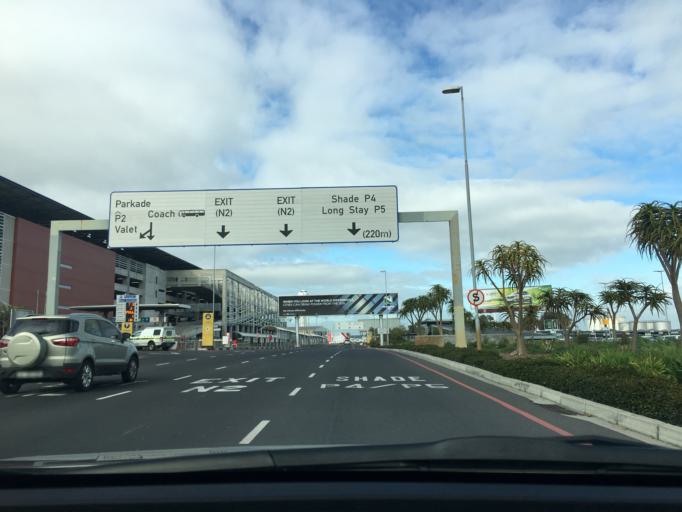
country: ZA
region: Western Cape
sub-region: City of Cape Town
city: Lansdowne
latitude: -33.9698
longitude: 18.5955
